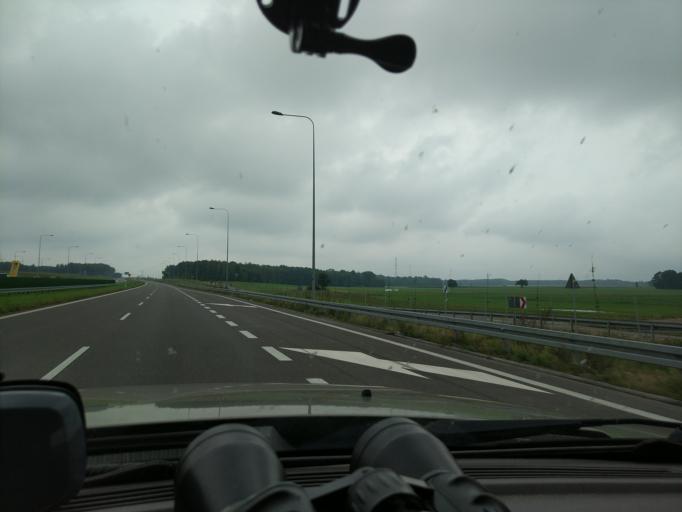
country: PL
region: Podlasie
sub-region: Powiat zambrowski
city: Rutki-Kossaki
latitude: 53.0379
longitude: 22.3543
